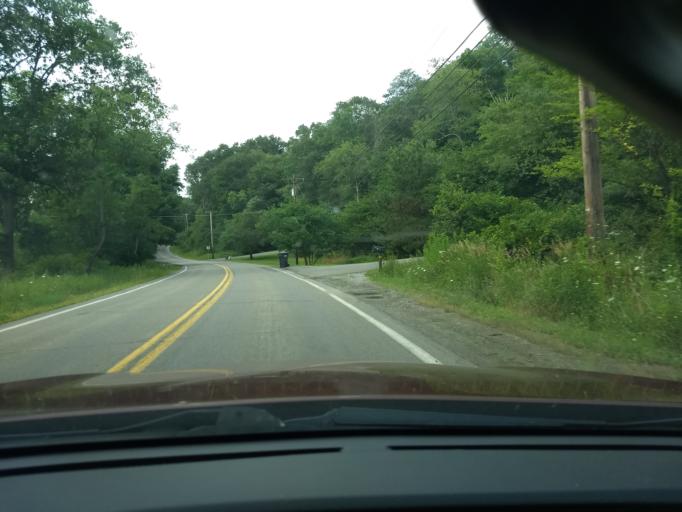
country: US
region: Pennsylvania
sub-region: Allegheny County
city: Bell Acres
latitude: 40.6373
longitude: -80.1386
